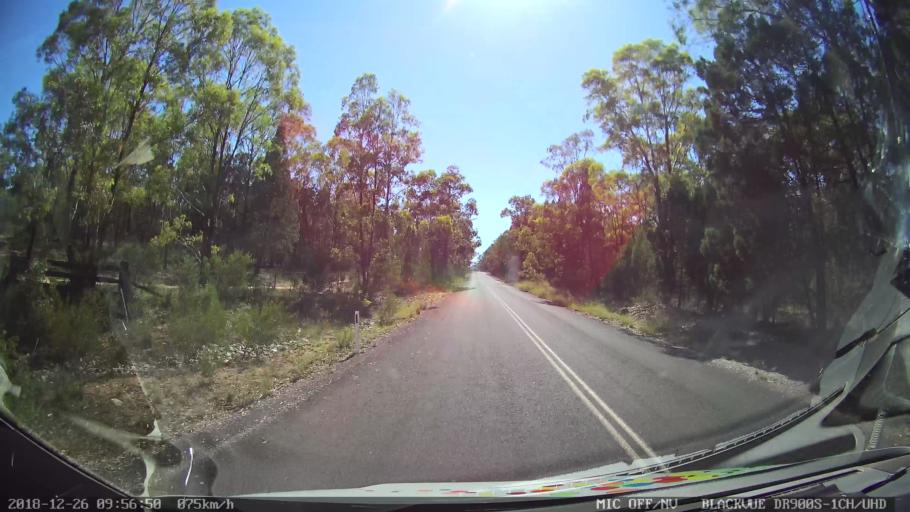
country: AU
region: New South Wales
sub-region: Mid-Western Regional
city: Kandos
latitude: -33.0400
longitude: 150.1845
